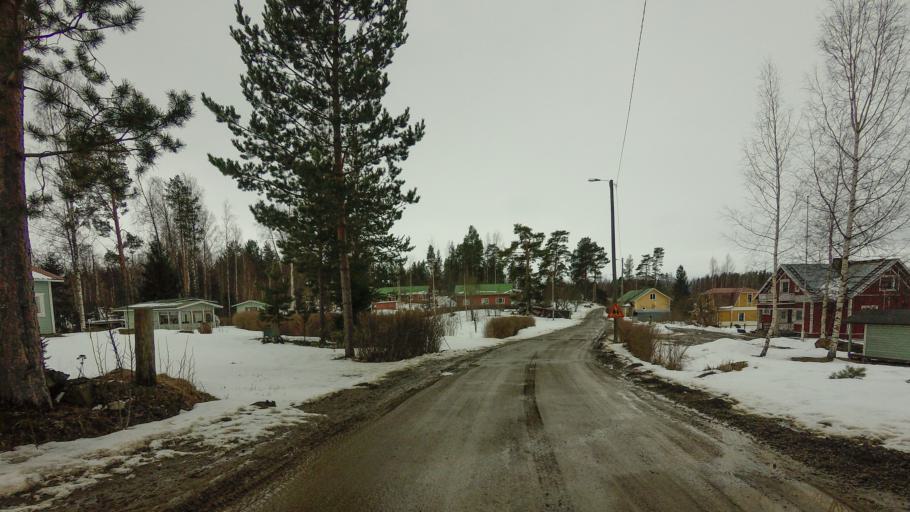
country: FI
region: Southern Savonia
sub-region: Savonlinna
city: Rantasalmi
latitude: 62.1153
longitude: 28.6096
